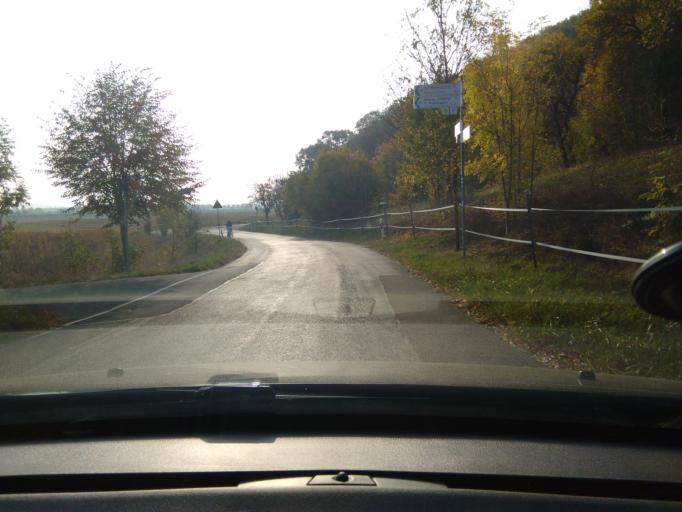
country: DE
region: Saxony
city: Niederau
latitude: 51.1502
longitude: 13.5177
